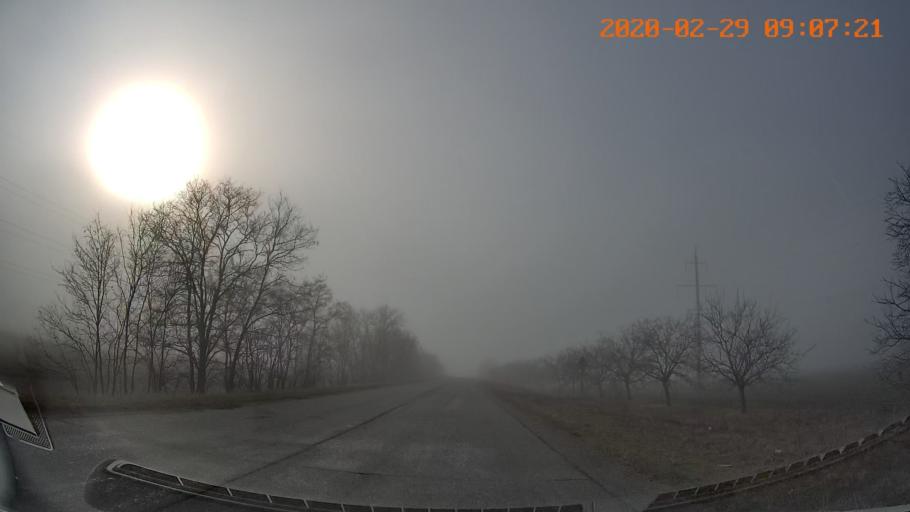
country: MD
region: Telenesti
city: Tiraspolul Nou
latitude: 46.8631
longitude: 29.7485
